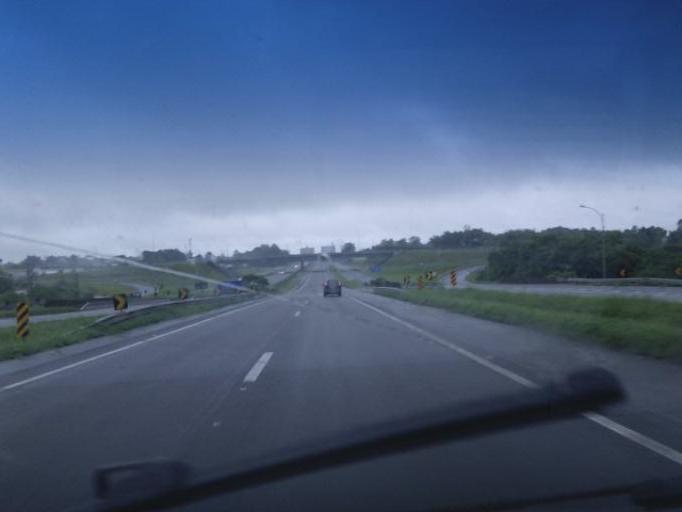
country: BR
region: Sao Paulo
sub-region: Registro
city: Registro
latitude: -24.5113
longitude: -47.8500
